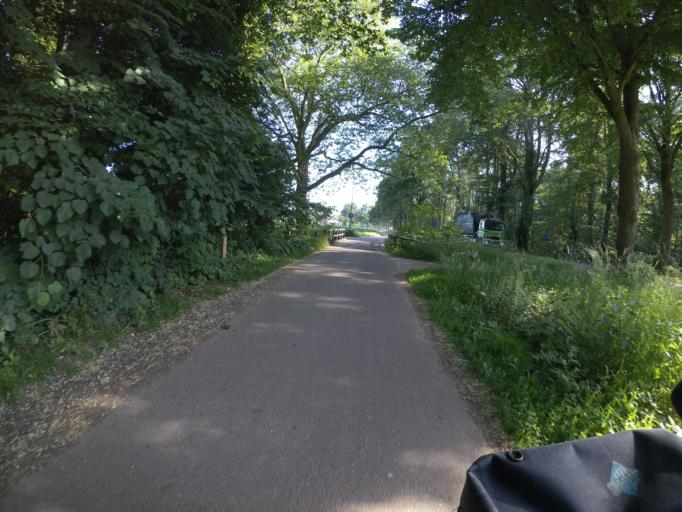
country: NL
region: Gelderland
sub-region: Gemeente Winterswijk
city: Winterswijk
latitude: 51.9879
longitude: 6.7270
